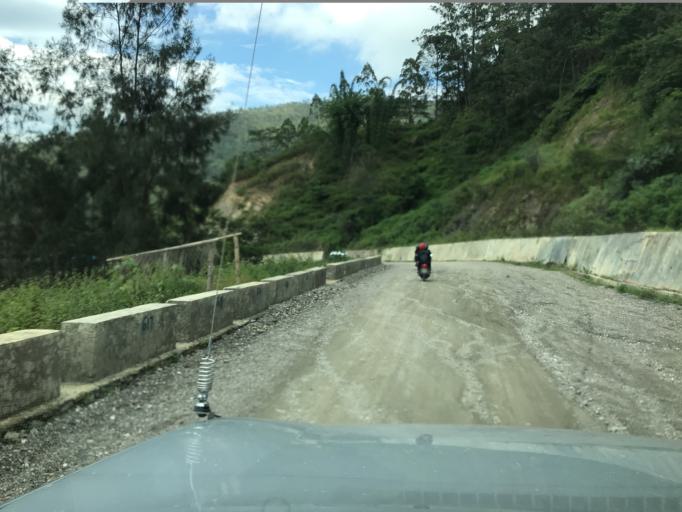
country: TL
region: Aileu
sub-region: Aileu Villa
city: Aileu
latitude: -8.6674
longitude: 125.5524
